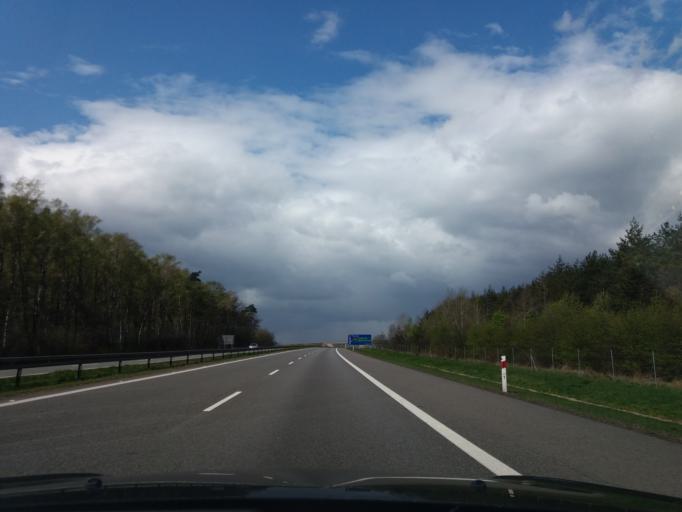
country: PL
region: Opole Voivodeship
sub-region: Powiat strzelecki
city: Strzelce Opolskie
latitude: 50.4535
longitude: 18.3004
